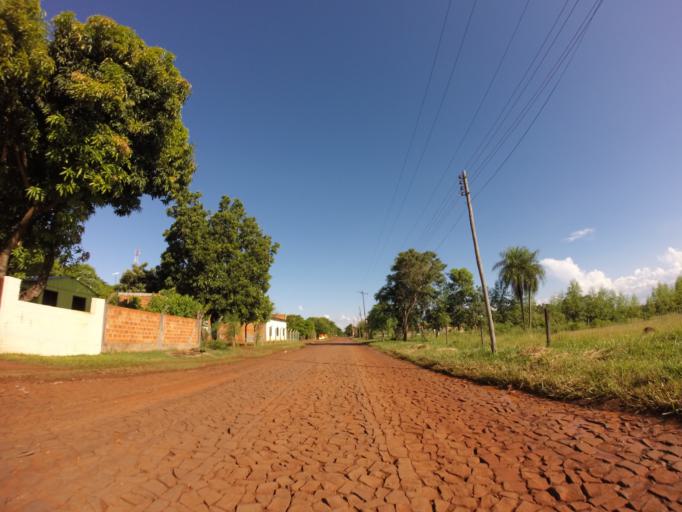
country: PY
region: Alto Parana
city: Ciudad del Este
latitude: -25.3900
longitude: -54.6508
